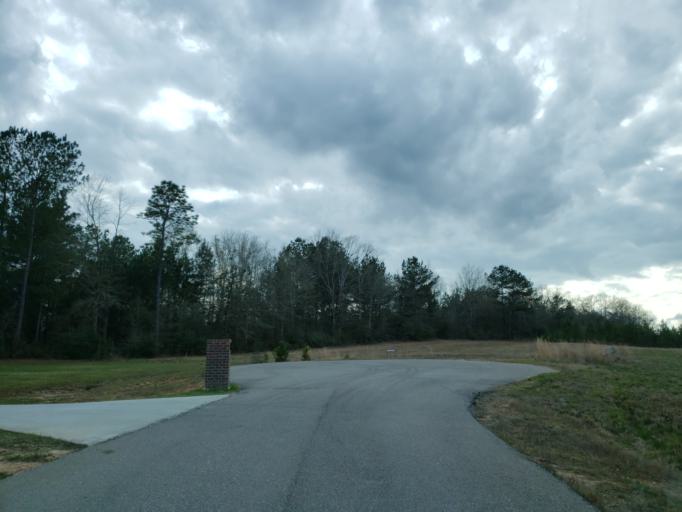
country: US
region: Mississippi
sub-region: Jones County
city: Ellisville
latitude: 31.5618
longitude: -89.2486
